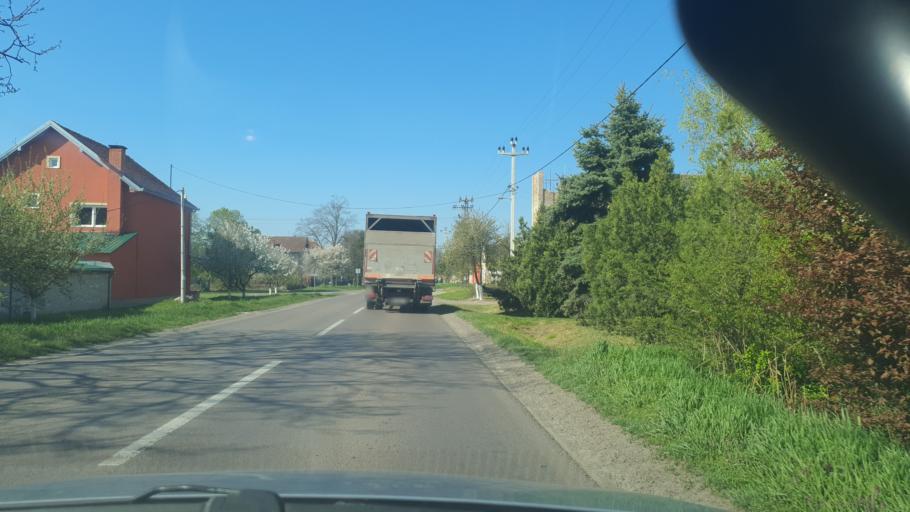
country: RS
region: Autonomna Pokrajina Vojvodina
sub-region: Zapadnobacki Okrug
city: Sombor
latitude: 45.7727
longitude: 19.2729
